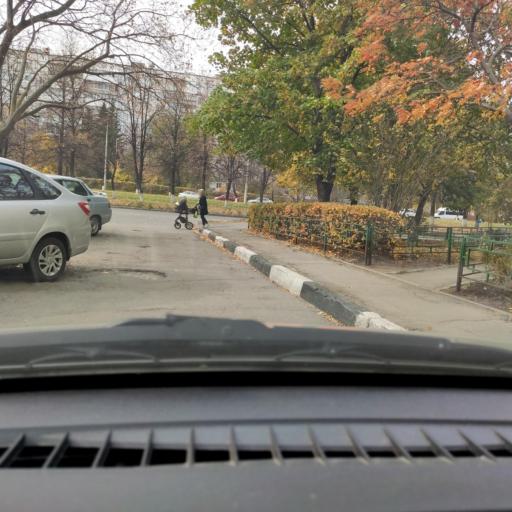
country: RU
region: Samara
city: Tol'yatti
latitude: 53.5204
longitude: 49.3113
